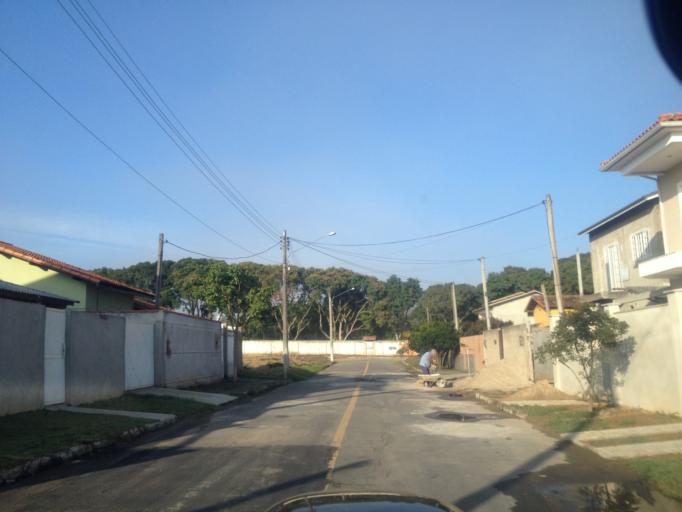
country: BR
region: Rio de Janeiro
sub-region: Porto Real
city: Porto Real
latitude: -22.4120
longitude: -44.3116
